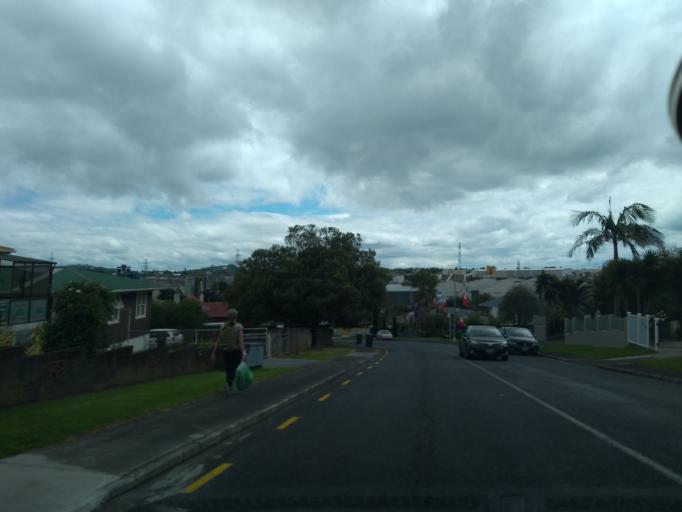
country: NZ
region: Auckland
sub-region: Auckland
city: Tamaki
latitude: -36.9094
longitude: 174.8224
